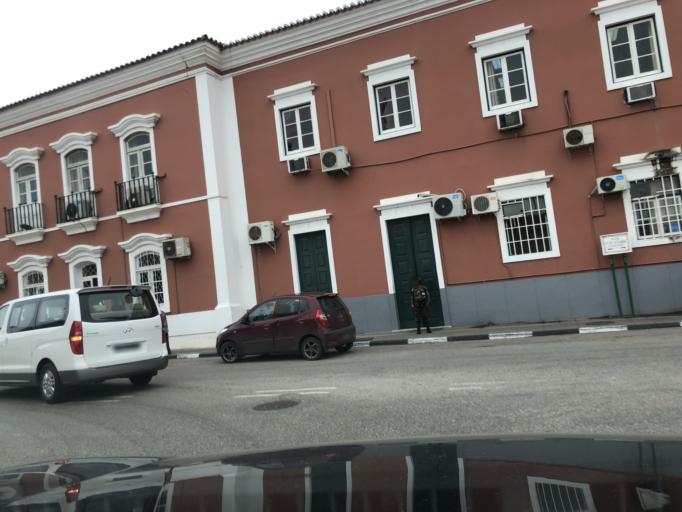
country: AO
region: Luanda
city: Luanda
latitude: -8.8182
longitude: 13.2253
